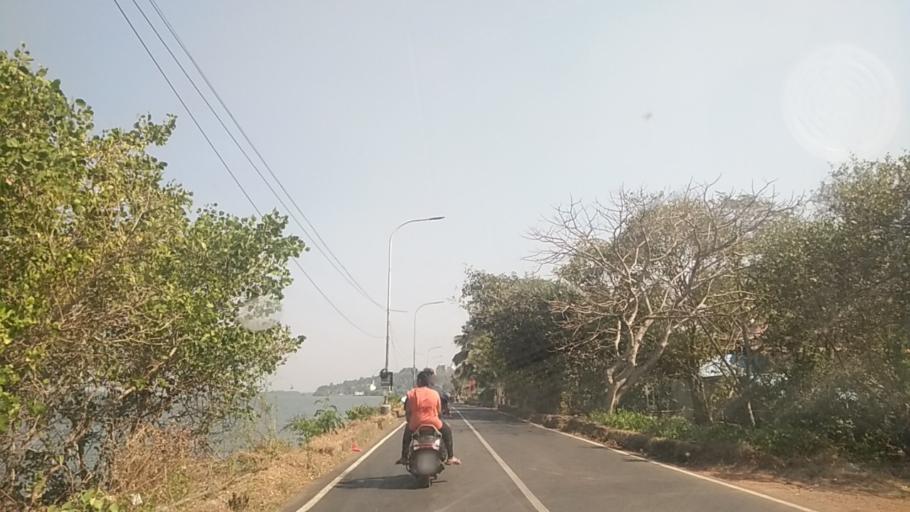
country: IN
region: Goa
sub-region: North Goa
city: Panaji
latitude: 15.5024
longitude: 73.8534
